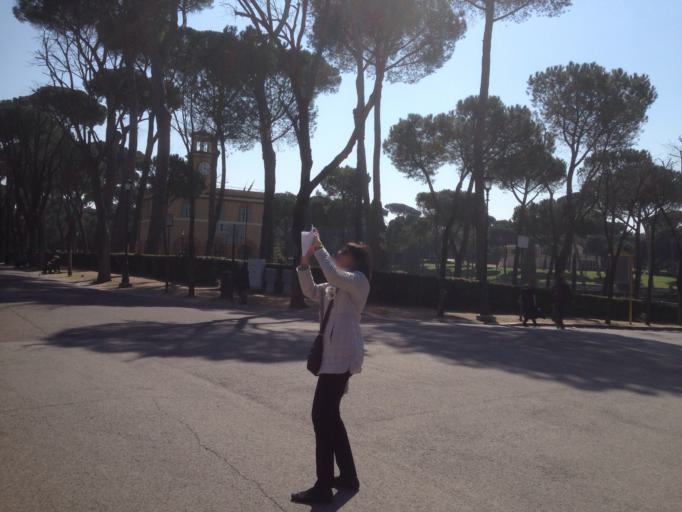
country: IT
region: Latium
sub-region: Citta metropolitana di Roma Capitale
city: Rome
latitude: 41.9152
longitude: 12.4871
